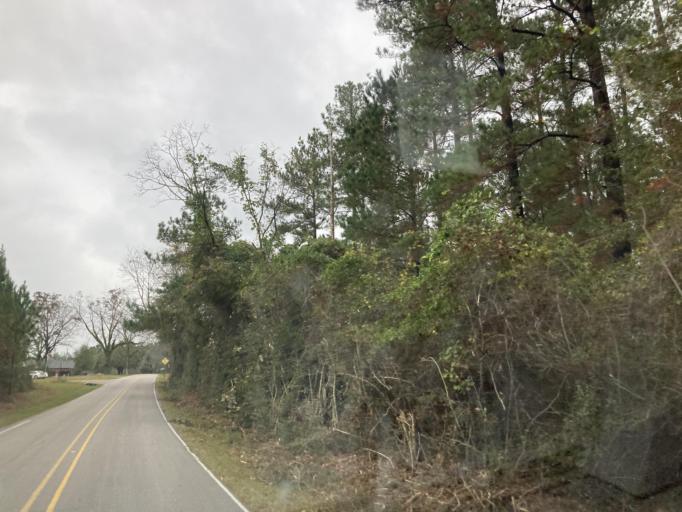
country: US
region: Mississippi
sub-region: Lamar County
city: Purvis
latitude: 31.1811
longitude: -89.4205
